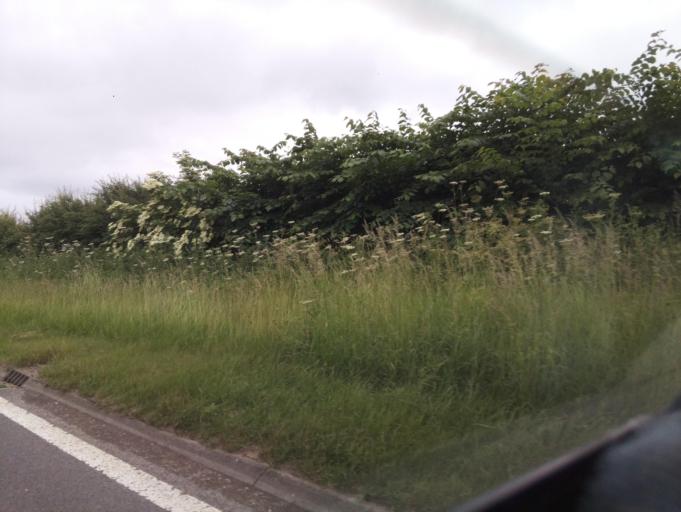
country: GB
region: England
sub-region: Derbyshire
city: Yeldersley
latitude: 52.9717
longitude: -1.6268
